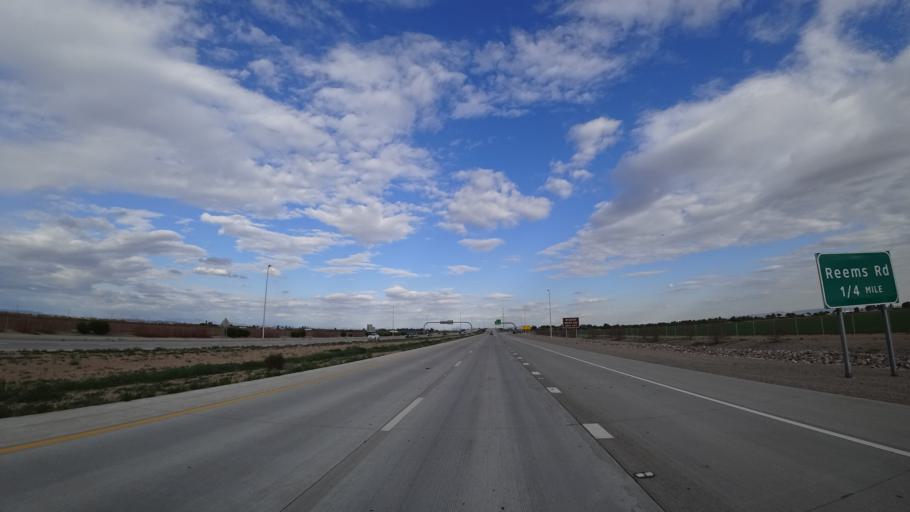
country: US
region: Arizona
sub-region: Maricopa County
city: Citrus Park
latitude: 33.5589
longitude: -112.4012
